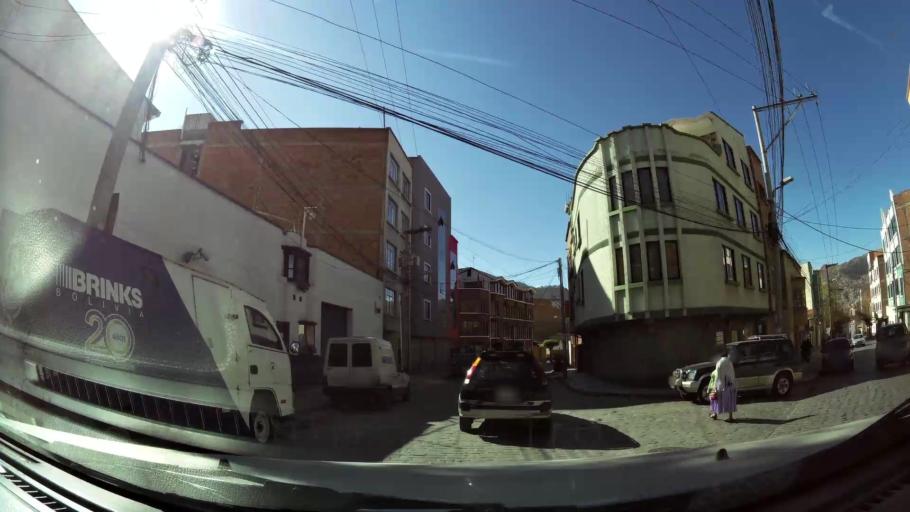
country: BO
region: La Paz
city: La Paz
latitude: -16.5083
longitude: -68.1347
